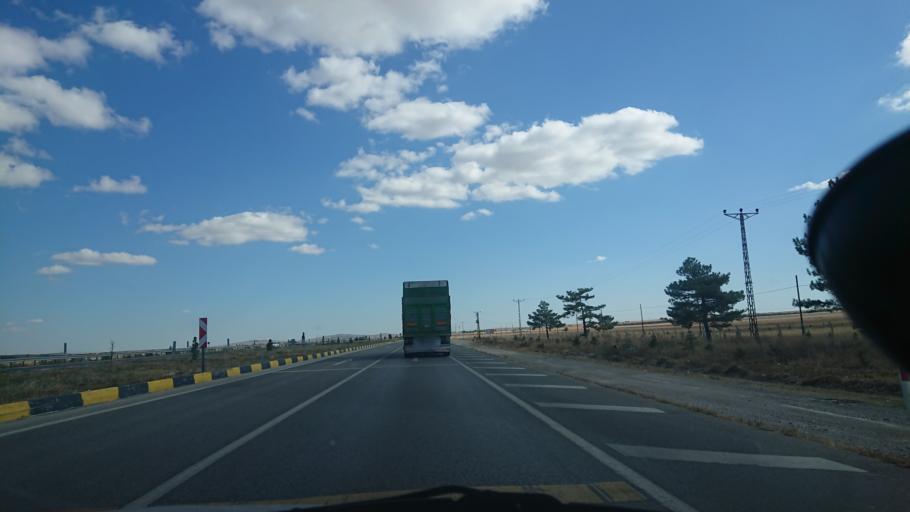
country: TR
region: Eskisehir
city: Mahmudiye
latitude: 39.5562
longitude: 30.9208
